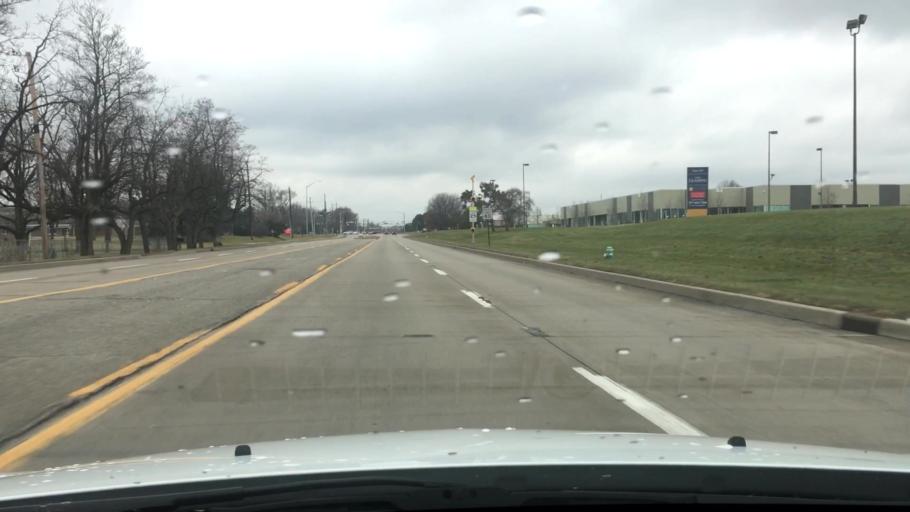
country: US
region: Indiana
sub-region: Boone County
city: Zionsville
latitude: 39.8819
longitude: -86.2545
